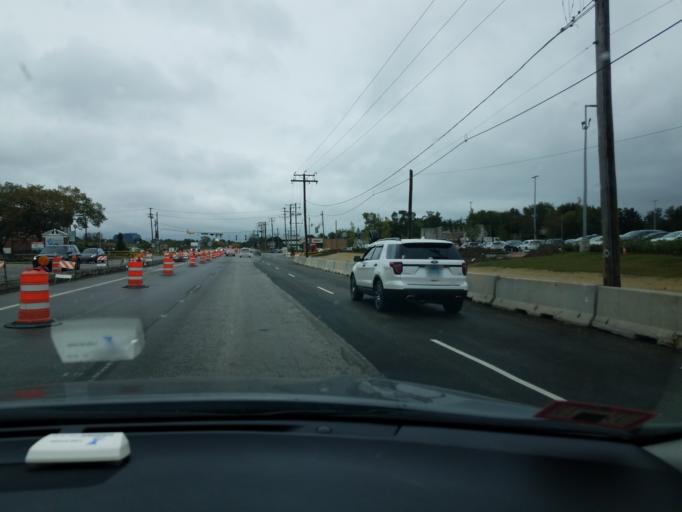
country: US
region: Illinois
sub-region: Lake County
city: Lincolnshire
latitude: 42.1692
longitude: -87.9223
